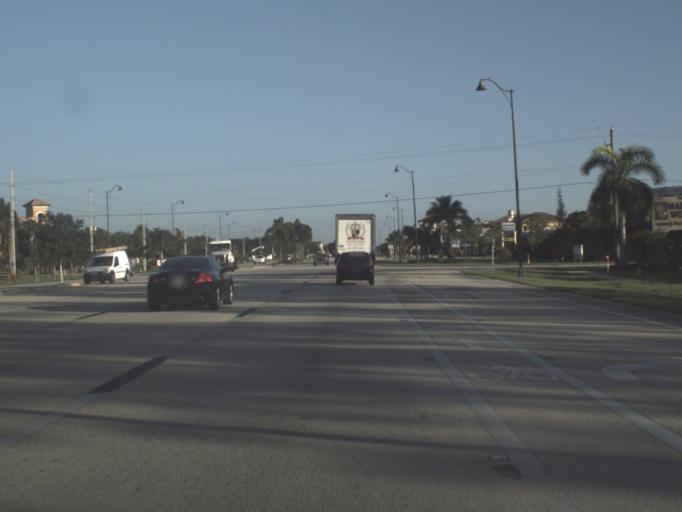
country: US
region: Florida
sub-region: Lee County
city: Estero
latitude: 26.3862
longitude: -81.8087
